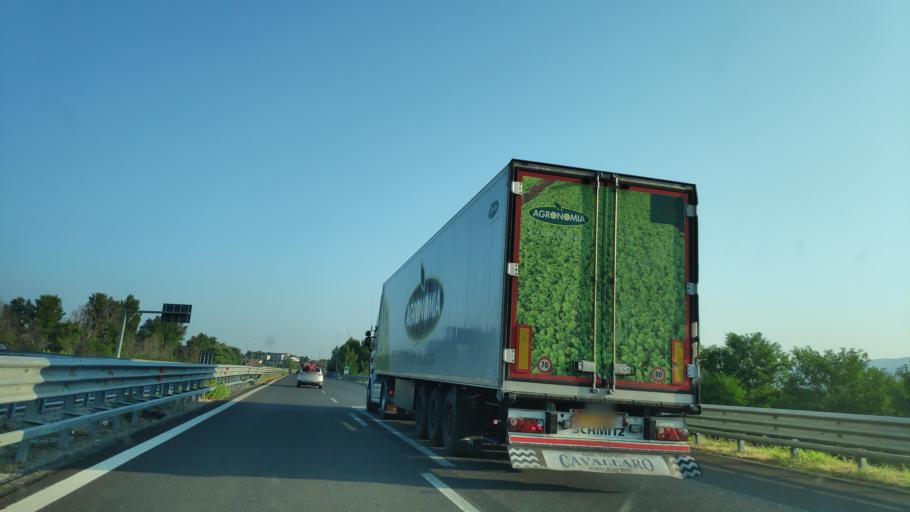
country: IT
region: Calabria
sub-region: Provincia di Cosenza
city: Quattromiglia
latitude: 39.3481
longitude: 16.2349
